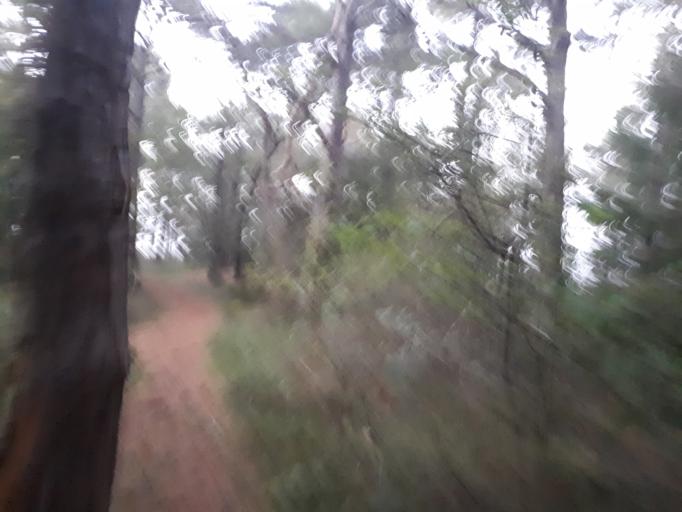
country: SE
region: Gotland
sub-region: Gotland
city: Visby
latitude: 57.6879
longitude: 18.3500
